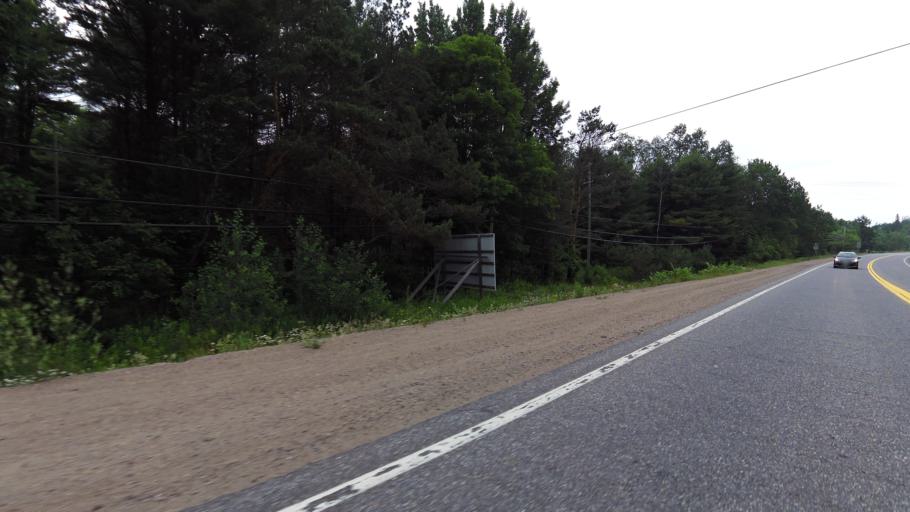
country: CA
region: Ontario
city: Huntsville
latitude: 45.3306
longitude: -79.0084
